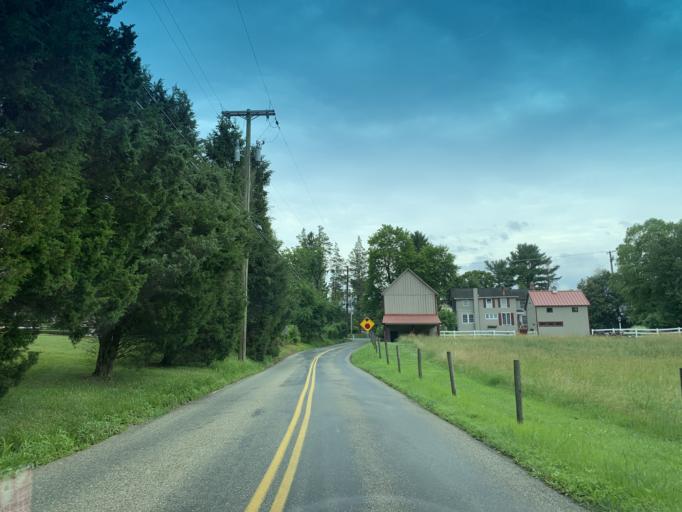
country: US
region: Maryland
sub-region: Harford County
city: Fallston
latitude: 39.5288
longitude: -76.4109
